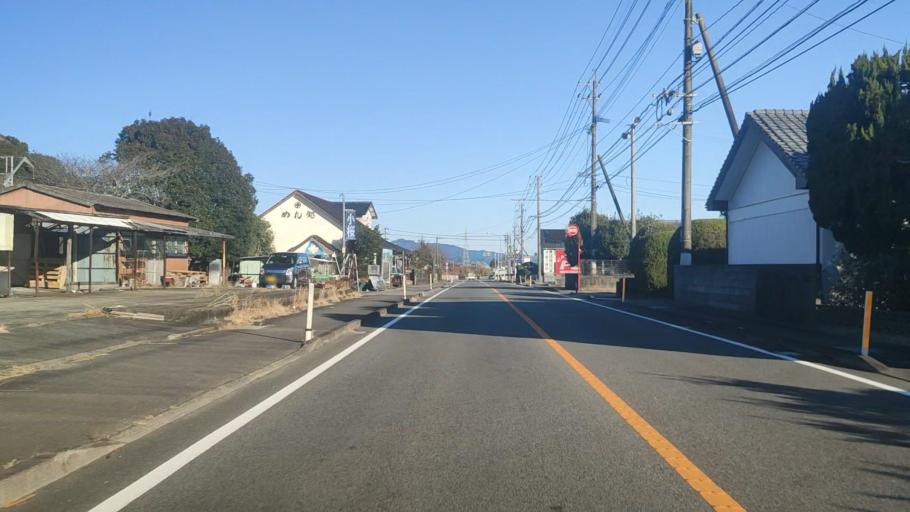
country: JP
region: Miyazaki
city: Nobeoka
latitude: 32.3864
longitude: 131.6275
